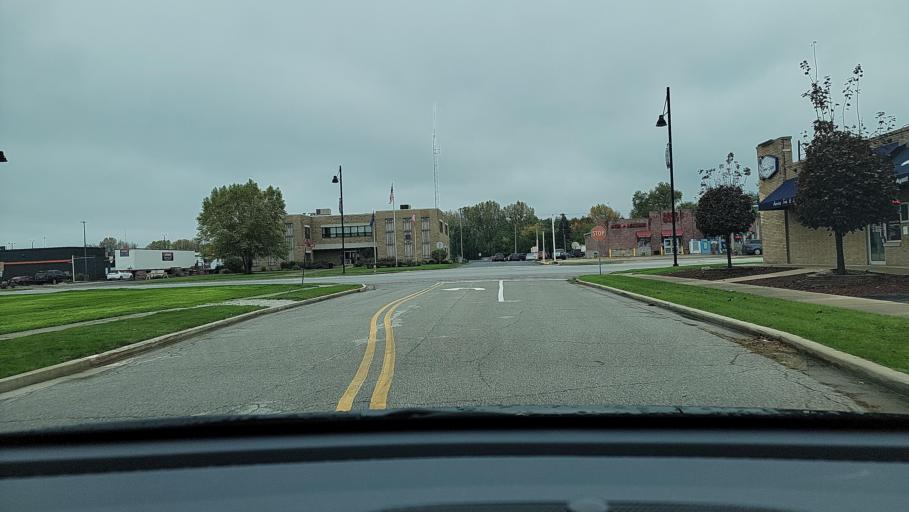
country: US
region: Indiana
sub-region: Porter County
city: Portage
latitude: 41.5753
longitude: -87.1799
